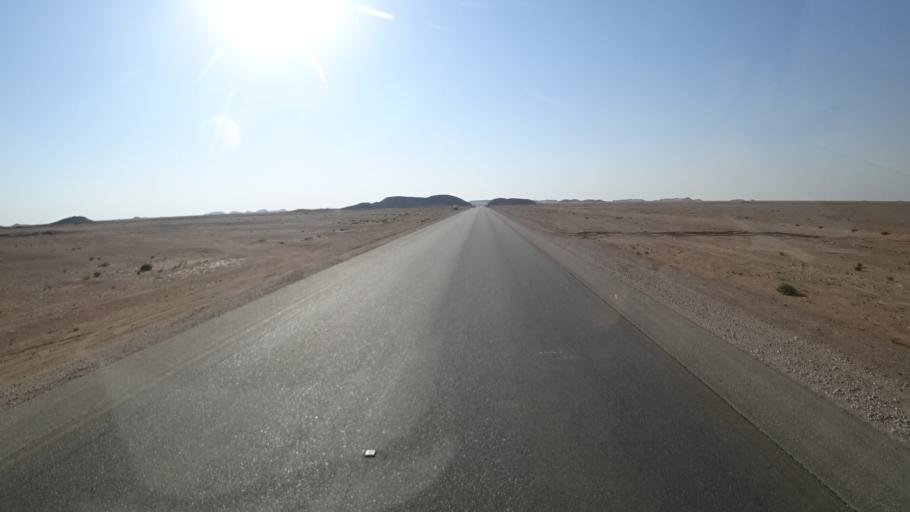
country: OM
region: Zufar
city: Salalah
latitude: 17.6398
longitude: 53.8970
